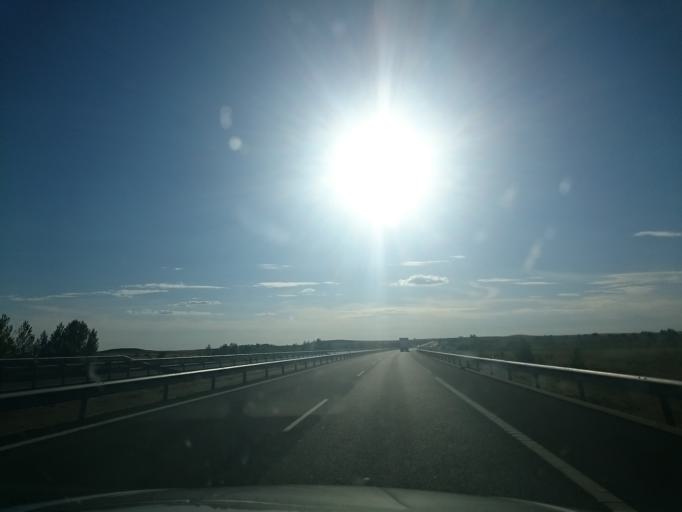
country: ES
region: Castille and Leon
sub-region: Provincia de Burgos
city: Villasandino
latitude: 42.3941
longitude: -4.1025
